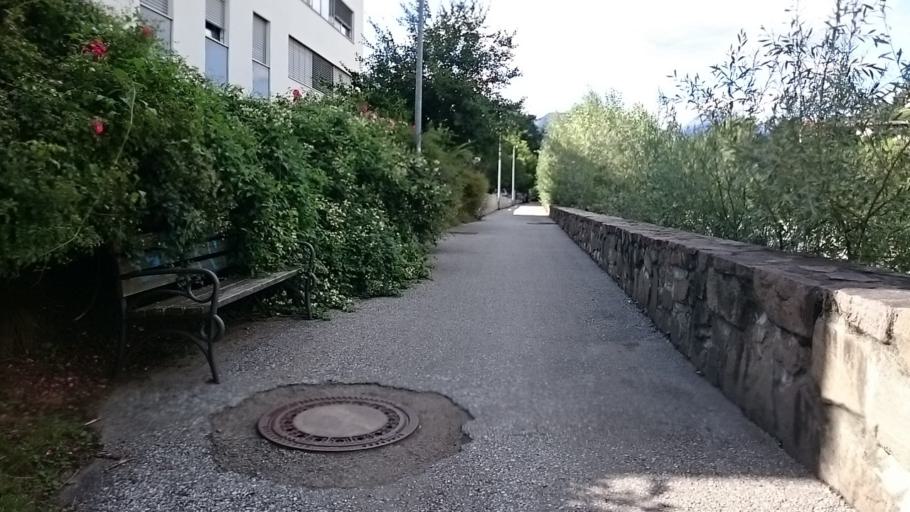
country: IT
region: Trentino-Alto Adige
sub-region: Bolzano
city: Bressanone
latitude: 46.7237
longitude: 11.6557
